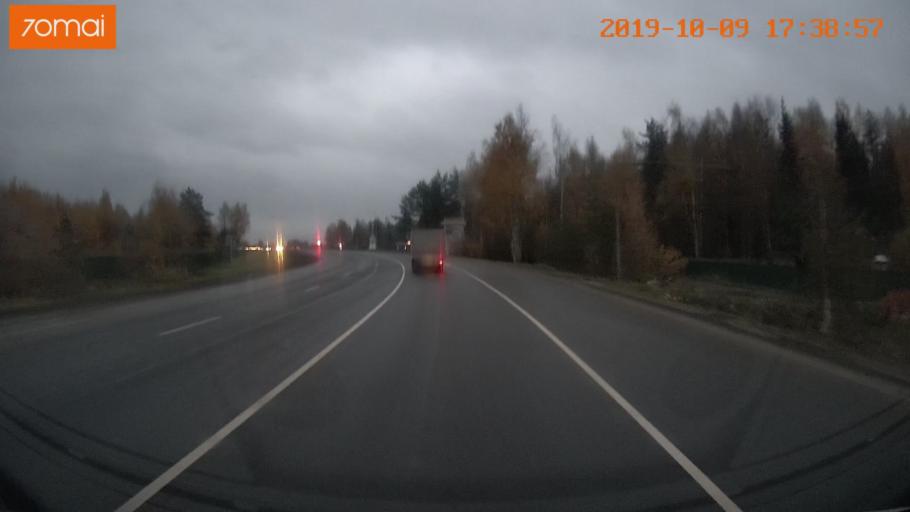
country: RU
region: Ivanovo
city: Bogorodskoye
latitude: 57.0653
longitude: 40.9529
